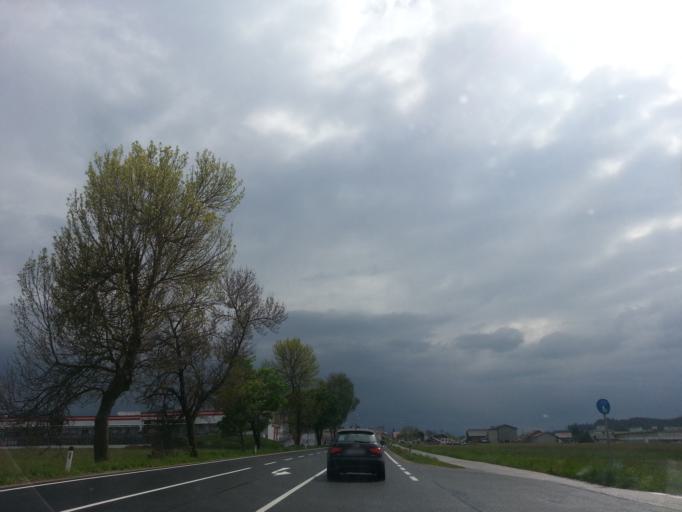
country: AT
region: Salzburg
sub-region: Politischer Bezirk Salzburg-Umgebung
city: Strasswalchen
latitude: 47.9653
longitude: 13.2445
